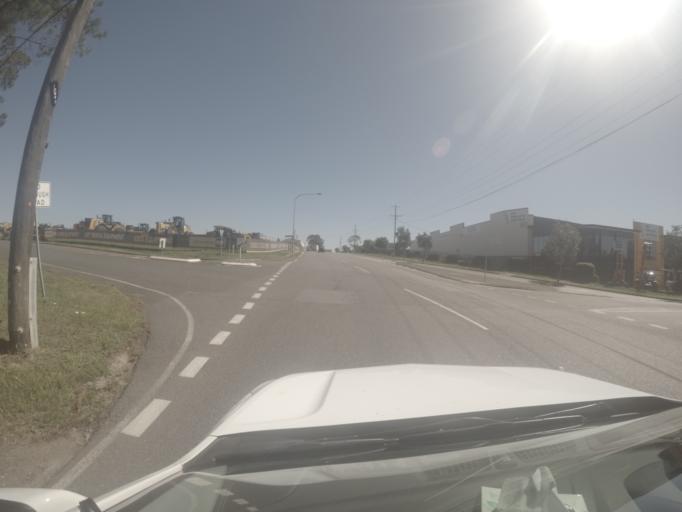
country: AU
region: Queensland
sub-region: Brisbane
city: Seventeen Mile Rocks
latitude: -27.5738
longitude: 152.9667
